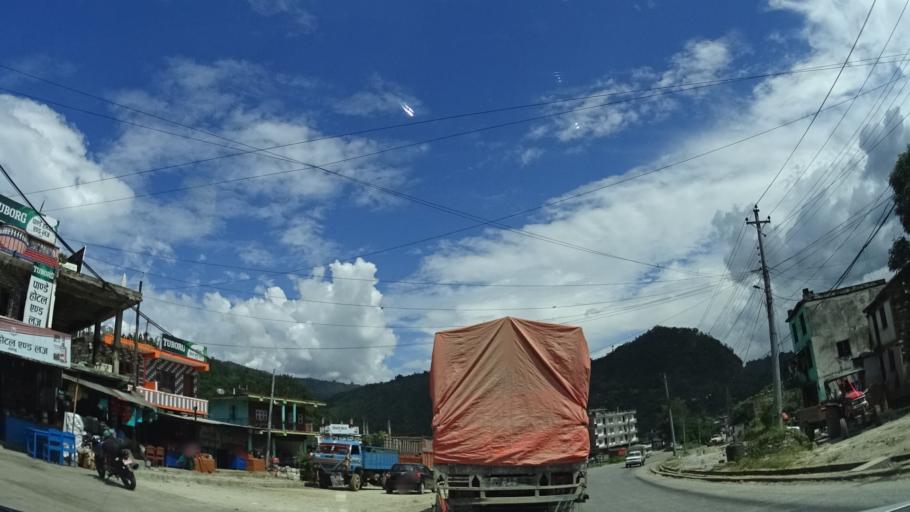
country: NP
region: Central Region
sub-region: Narayani Zone
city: Bharatpur
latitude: 27.8139
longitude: 84.8292
